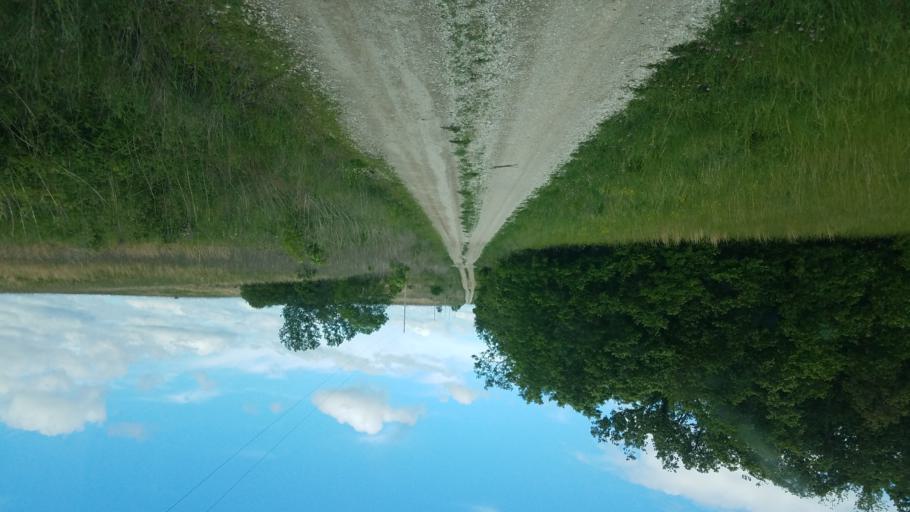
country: US
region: Missouri
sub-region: Mercer County
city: Princeton
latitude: 40.2602
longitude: -93.7061
